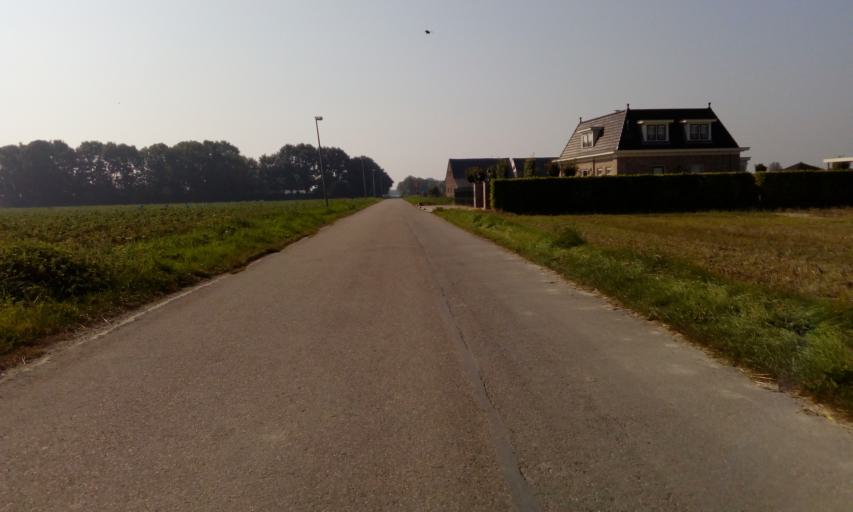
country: NL
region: South Holland
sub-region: Gemeente Rijnwoude
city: Benthuizen
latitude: 52.0517
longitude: 4.5914
